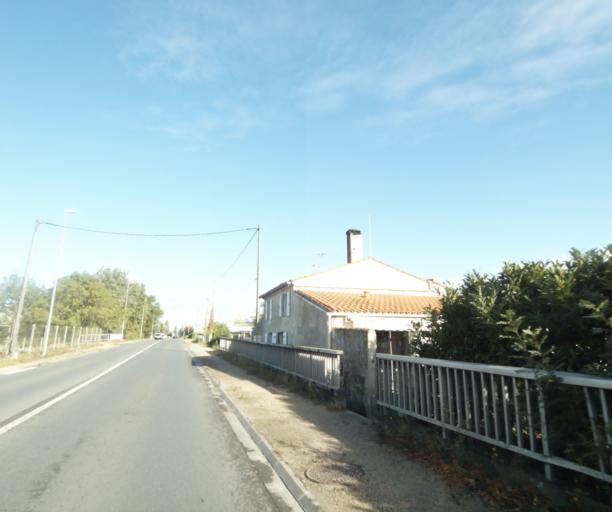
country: FR
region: Poitou-Charentes
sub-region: Departement de la Charente-Maritime
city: Tonnay-Charente
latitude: 45.9520
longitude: -0.9333
